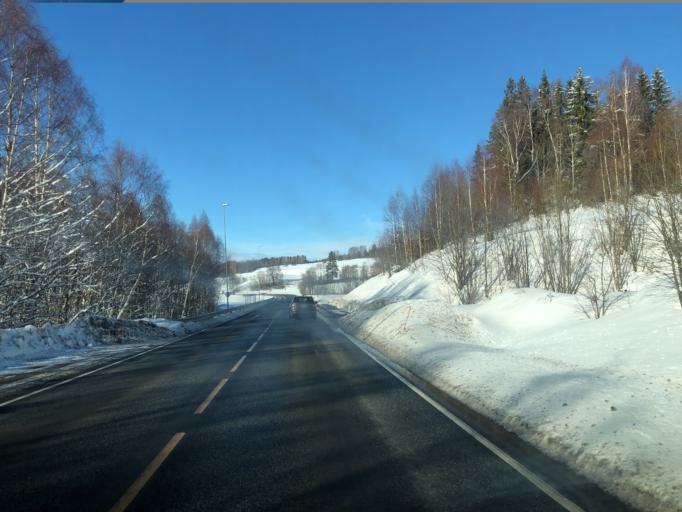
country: NO
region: Oppland
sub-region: Lunner
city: Roa
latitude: 60.3098
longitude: 10.5955
